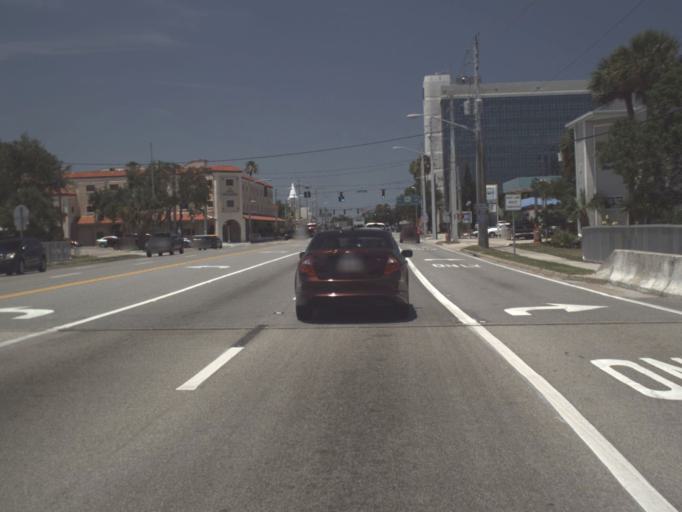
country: US
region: Florida
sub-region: Brevard County
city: Melbourne
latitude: 28.0778
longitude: -80.6024
